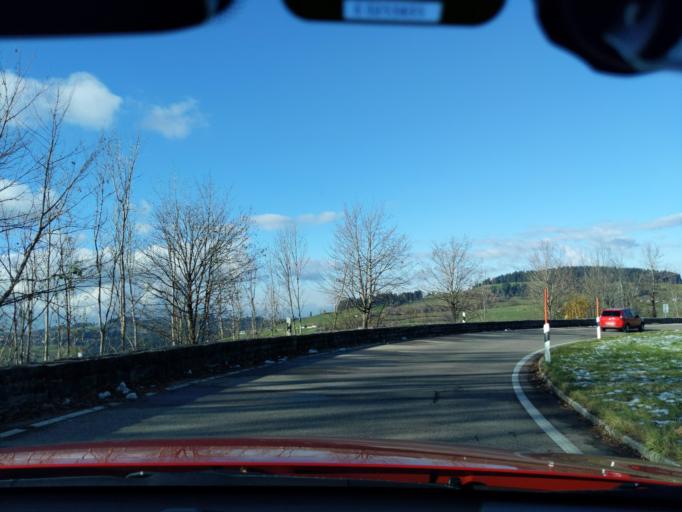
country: DE
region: Bavaria
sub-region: Swabia
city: Oberstaufen
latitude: 47.5427
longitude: 9.9883
